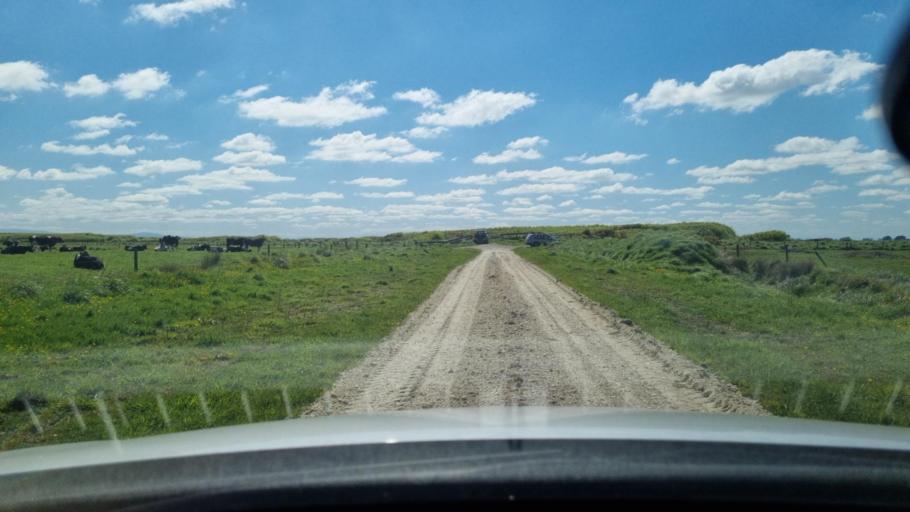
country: NZ
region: Southland
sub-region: Invercargill City
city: Invercargill
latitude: -46.3853
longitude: 168.2570
